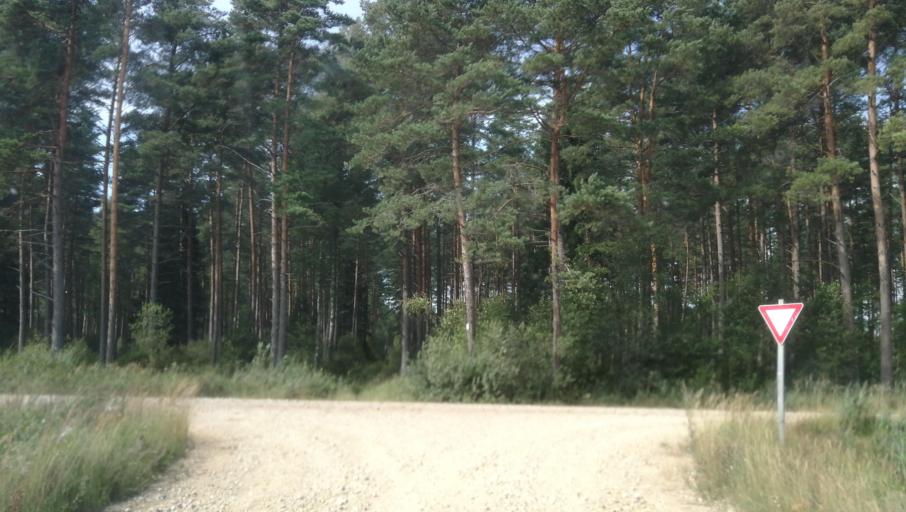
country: LV
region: Pavilostas
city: Pavilosta
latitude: 56.8194
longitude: 21.2895
